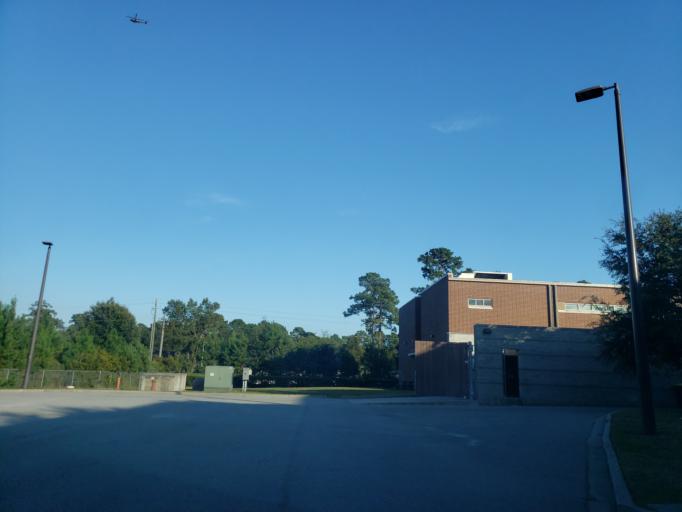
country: US
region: Georgia
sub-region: Chatham County
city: Isle of Hope
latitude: 31.9962
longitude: -81.0761
